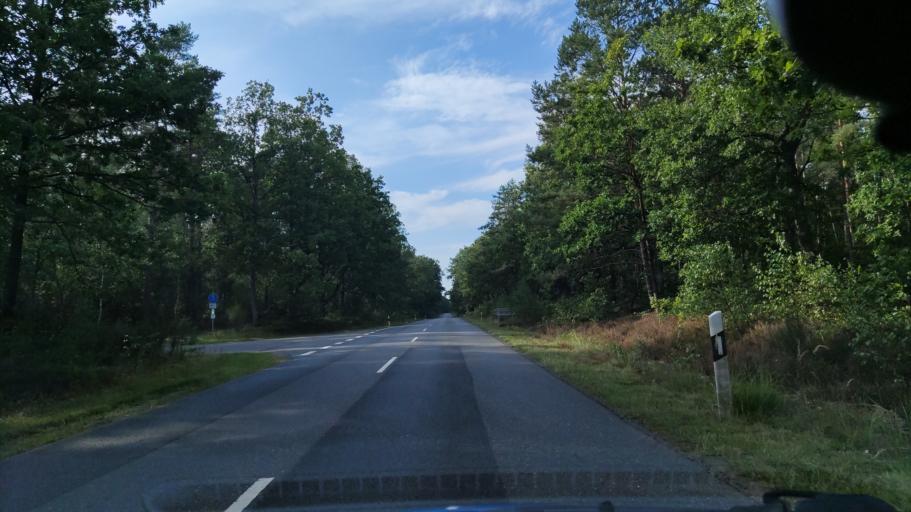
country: DE
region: Lower Saxony
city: Fassberg
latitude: 52.9662
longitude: 10.1696
